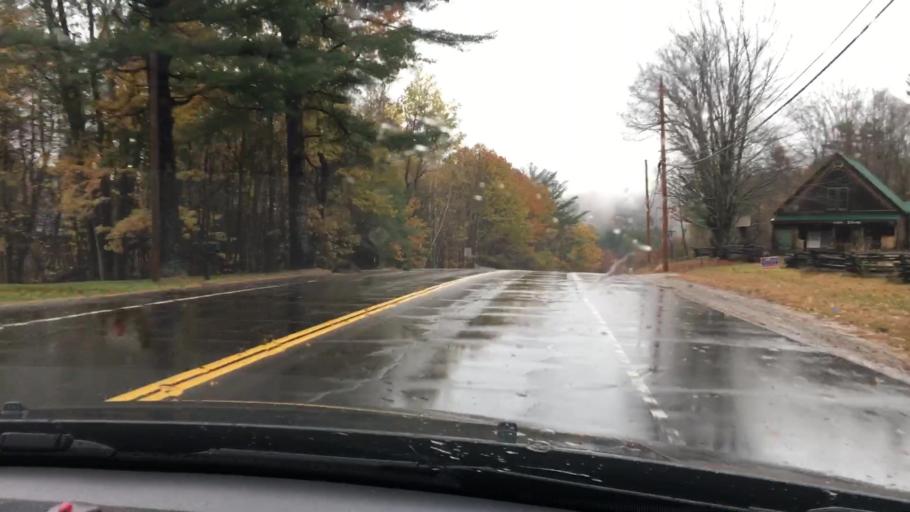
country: US
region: New Hampshire
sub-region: Grafton County
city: Holderness
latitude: 43.7221
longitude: -71.6132
